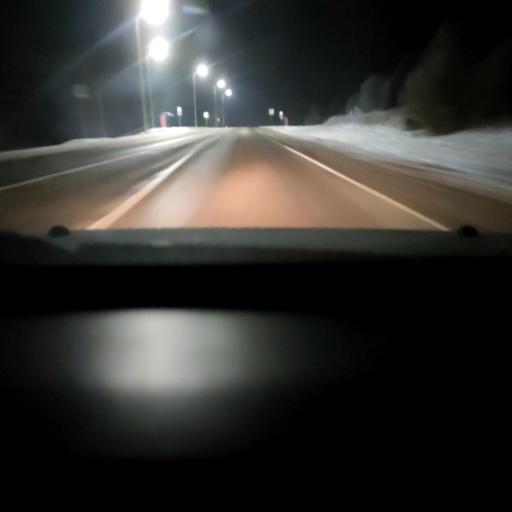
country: RU
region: Perm
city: Pavlovskiy
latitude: 57.8908
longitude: 54.9354
